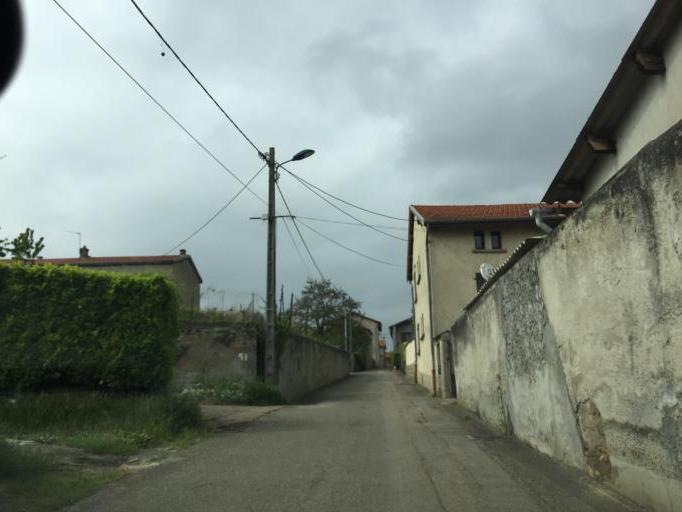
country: FR
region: Rhone-Alpes
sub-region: Departement de l'Ain
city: Miribel
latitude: 45.8287
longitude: 4.9438
